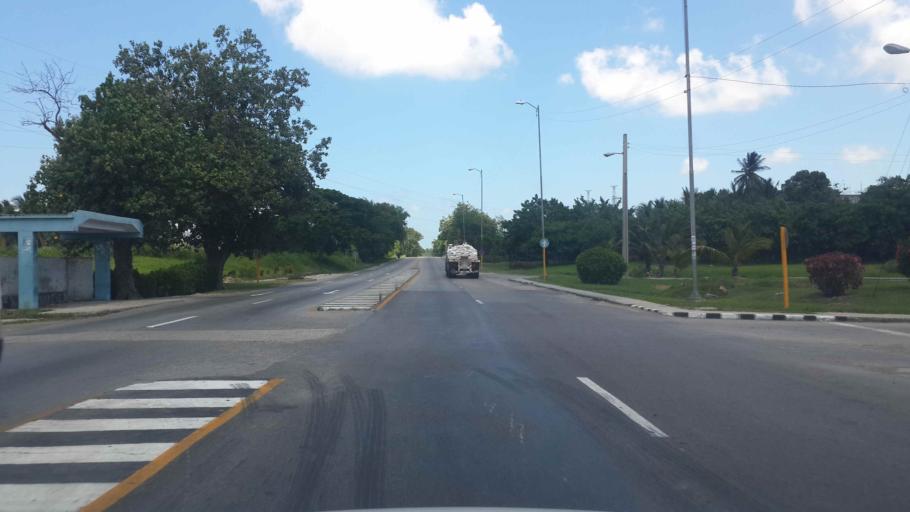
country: CU
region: La Habana
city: Guanabacoa
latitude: 23.1369
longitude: -82.3077
